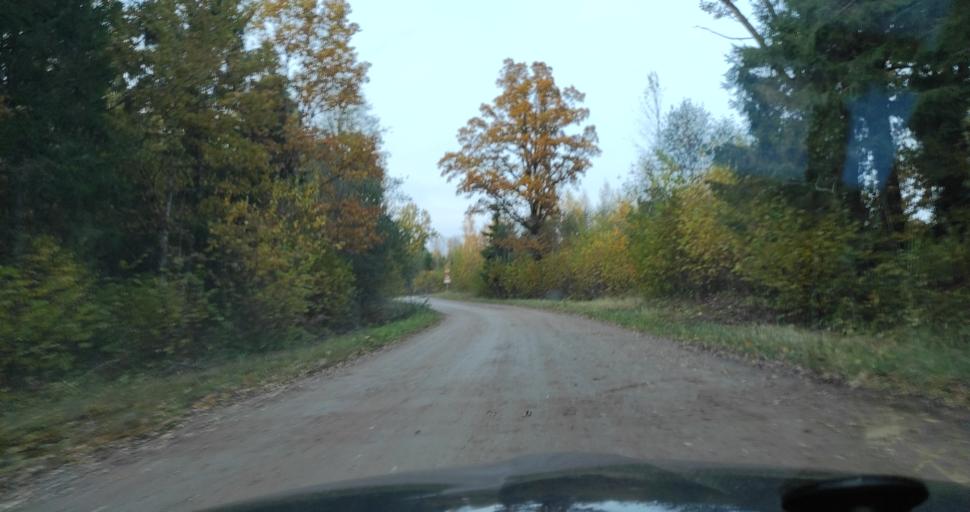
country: LV
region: Vainode
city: Vainode
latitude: 56.6230
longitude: 21.8165
